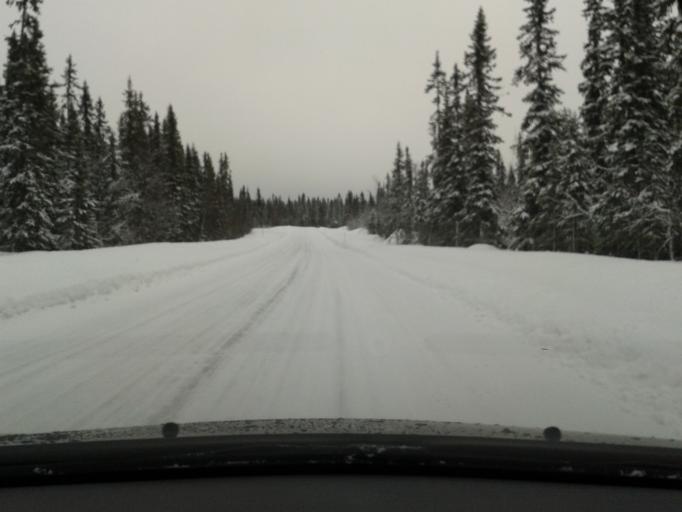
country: SE
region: Vaesterbotten
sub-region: Vilhelmina Kommun
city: Sjoberg
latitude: 65.1197
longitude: 15.8797
